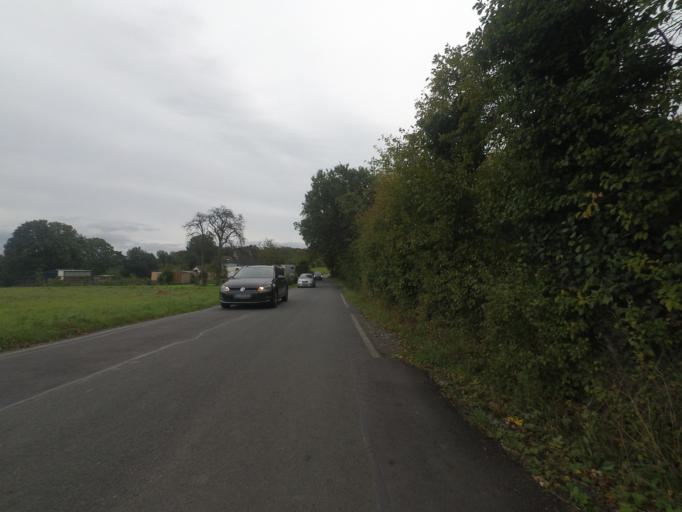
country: DE
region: North Rhine-Westphalia
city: Iserlohn
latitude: 51.4061
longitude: 7.6759
